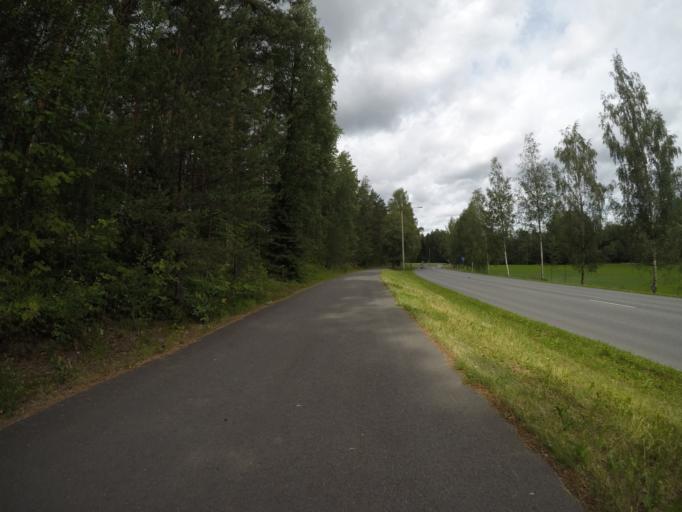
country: FI
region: Haeme
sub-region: Haemeenlinna
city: Haemeenlinna
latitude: 60.9700
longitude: 24.4371
